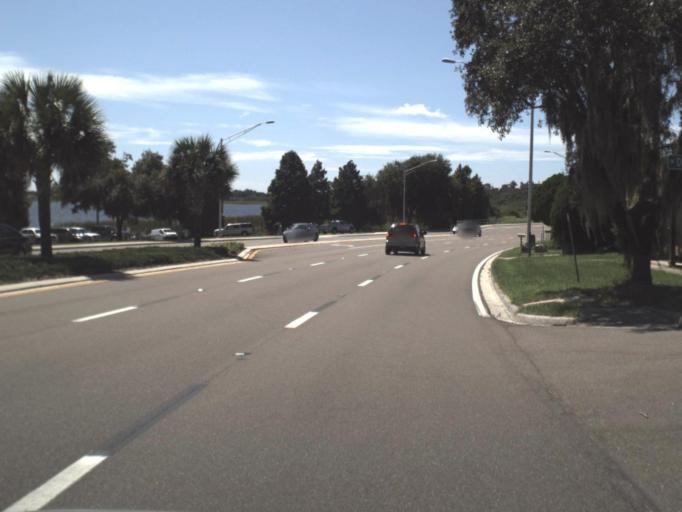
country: US
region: Florida
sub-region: Polk County
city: Lake Alfred
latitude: 28.0790
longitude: -81.7299
